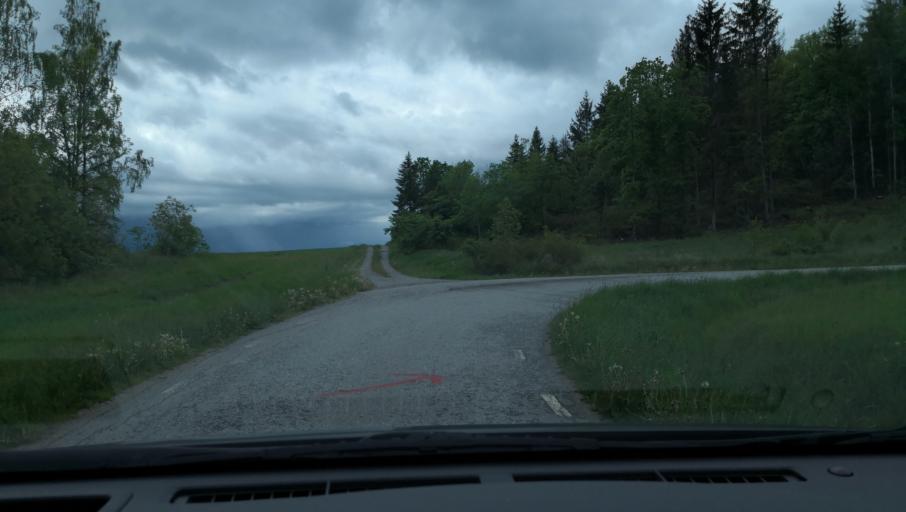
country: SE
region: Uppsala
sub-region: Enkopings Kommun
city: Orsundsbro
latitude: 59.7226
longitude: 17.3834
